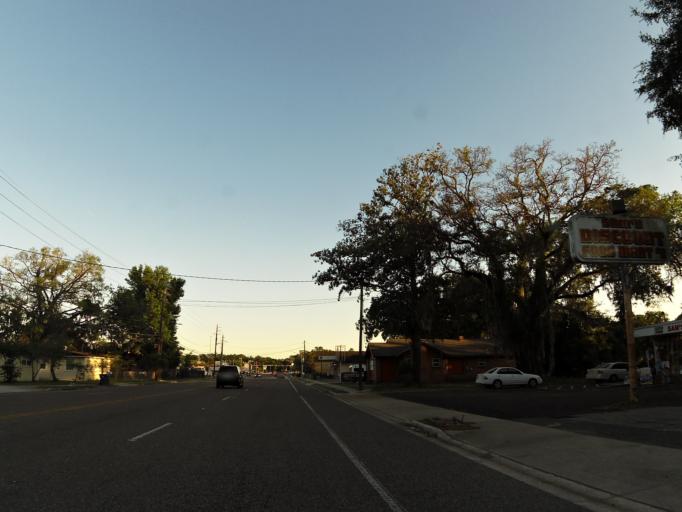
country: US
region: Florida
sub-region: Duval County
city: Jacksonville
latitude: 30.3168
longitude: -81.5794
